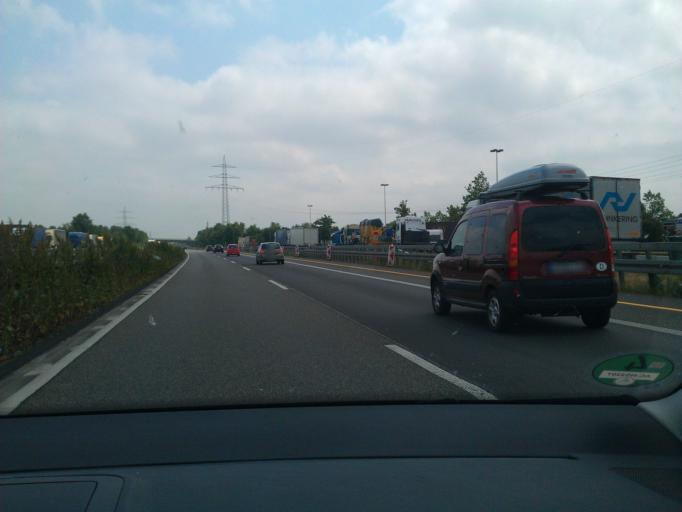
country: DE
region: North Rhine-Westphalia
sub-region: Regierungsbezirk Koln
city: Rheinbach
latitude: 50.6444
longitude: 6.9409
